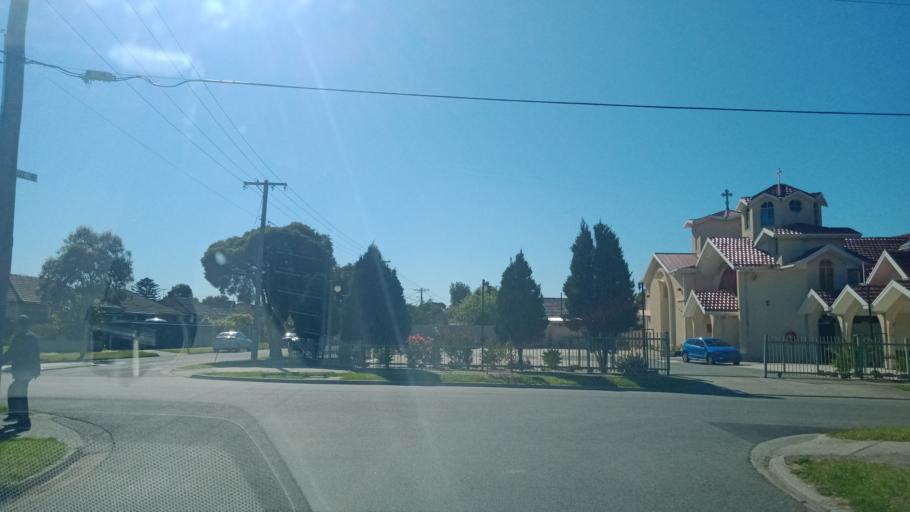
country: AU
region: Victoria
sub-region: Greater Dandenong
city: Springvale
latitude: -37.9356
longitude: 145.1689
